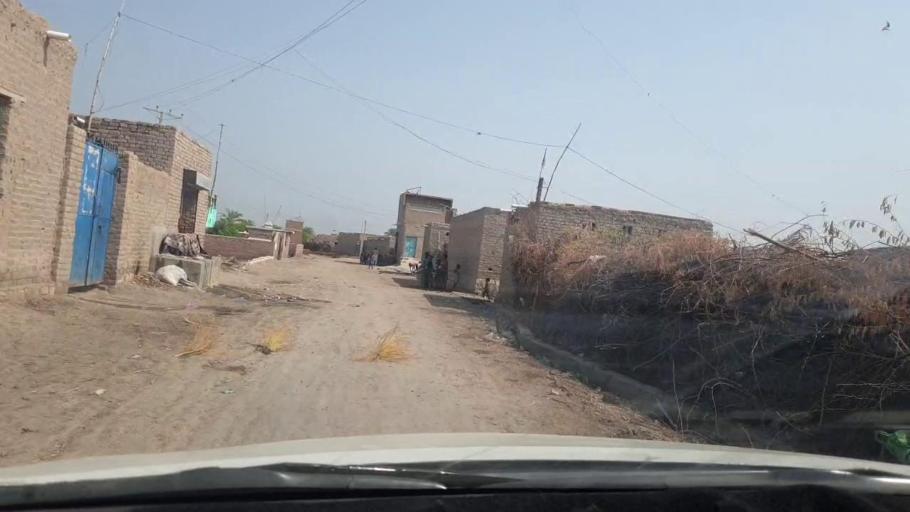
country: PK
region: Sindh
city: Rohri
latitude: 27.6292
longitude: 68.8864
